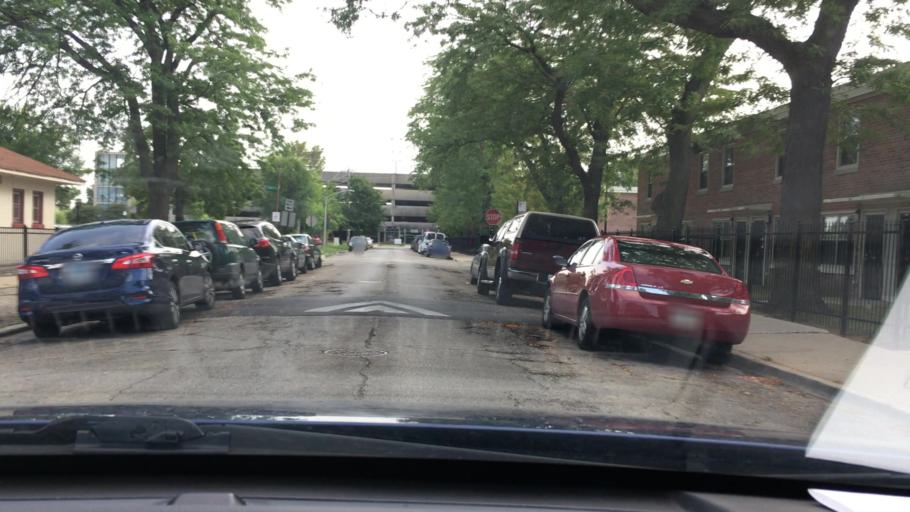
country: US
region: Illinois
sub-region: Cook County
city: Chicago
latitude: 41.8461
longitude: -87.6928
